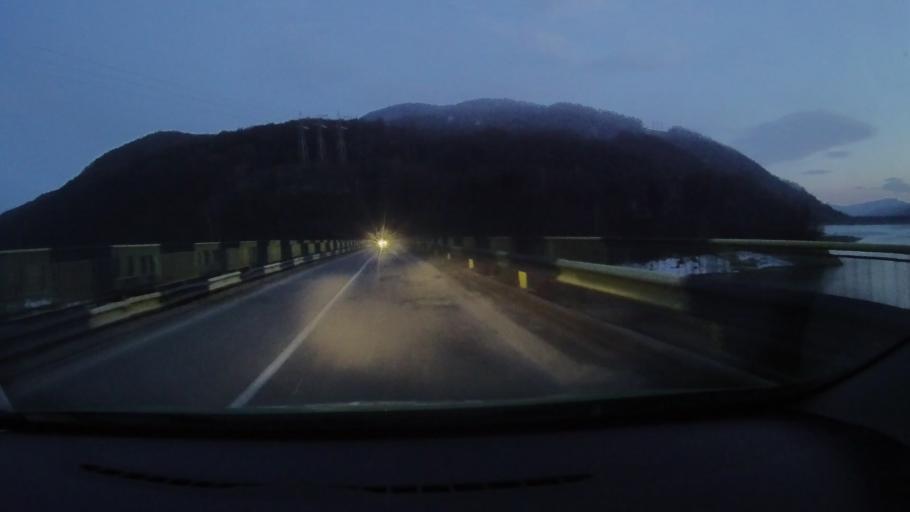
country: RO
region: Prahova
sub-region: Comuna Sotrile
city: Sotrile
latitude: 45.2547
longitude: 25.7418
